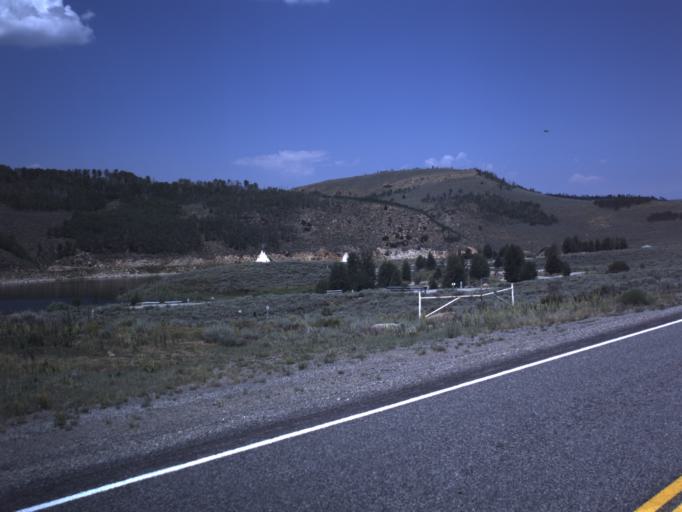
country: US
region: Utah
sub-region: Carbon County
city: Helper
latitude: 39.8123
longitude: -111.1352
